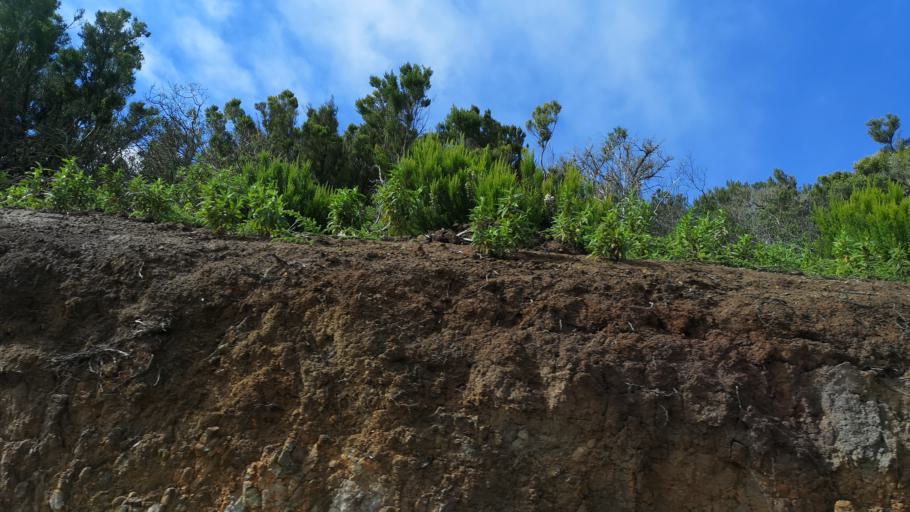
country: ES
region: Canary Islands
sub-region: Provincia de Santa Cruz de Tenerife
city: Vallehermosa
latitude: 28.1458
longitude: -17.3085
